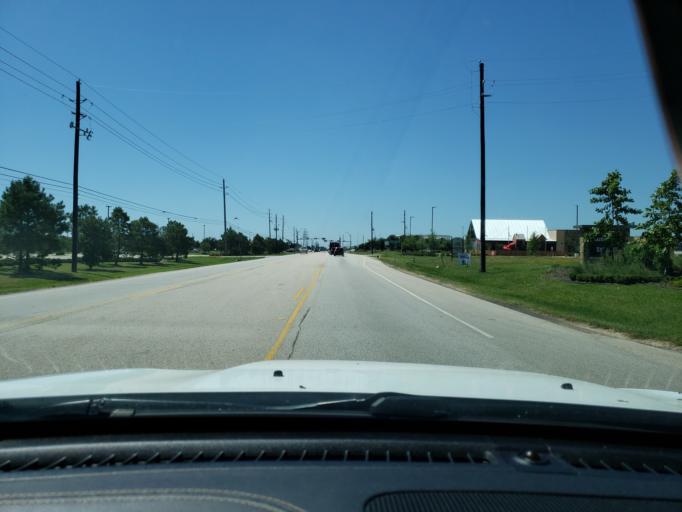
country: US
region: Texas
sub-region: Fort Bend County
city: Fulshear
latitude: 29.7087
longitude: -95.8462
